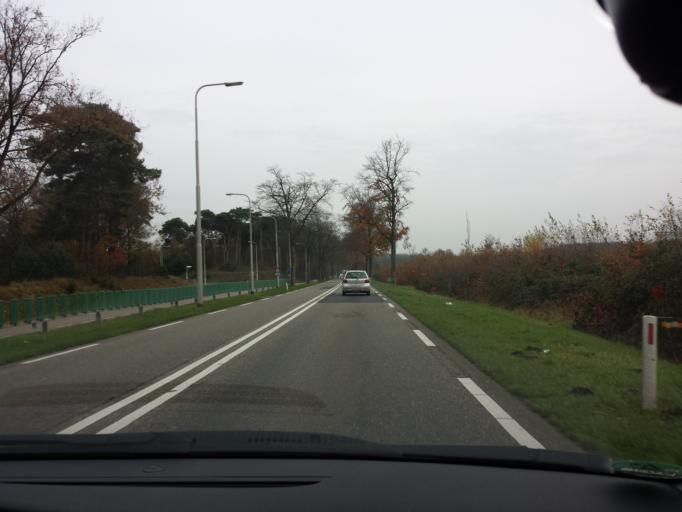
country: NL
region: Limburg
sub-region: Gemeente Leudal
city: Heythuysen
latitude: 51.1961
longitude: 5.8855
